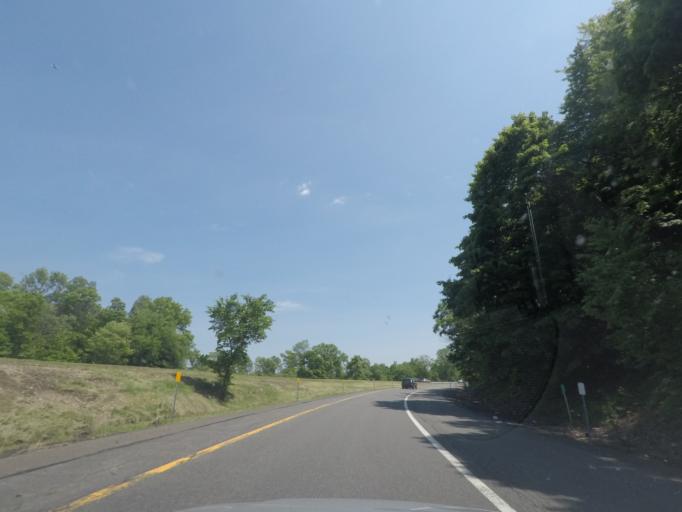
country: US
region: New York
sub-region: Rockland County
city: Spring Valley
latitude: 41.0964
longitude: -74.0409
